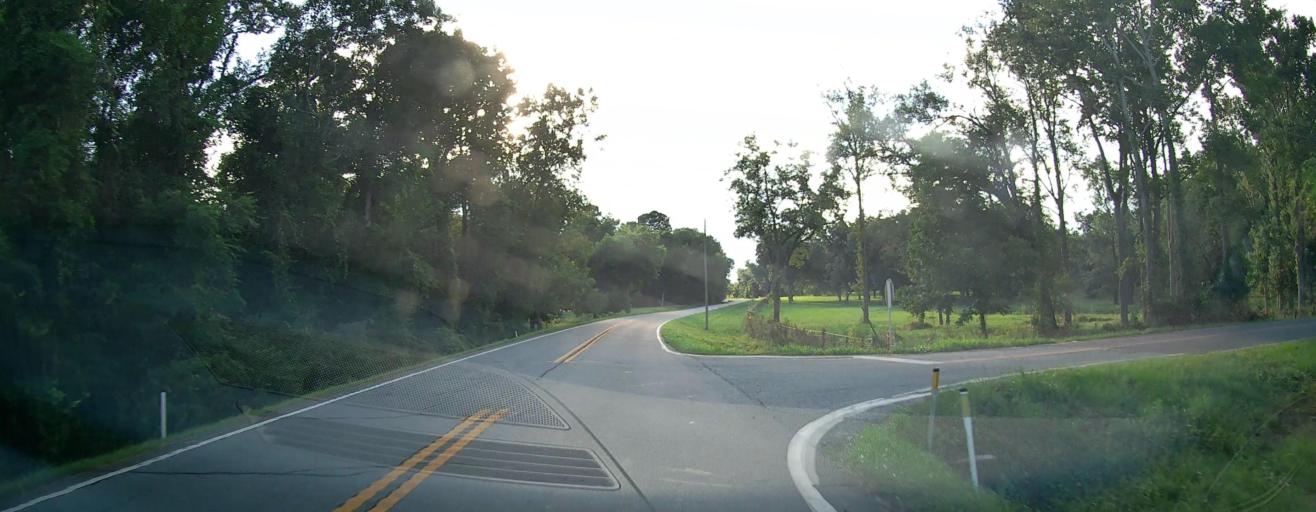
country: US
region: Georgia
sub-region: Pulaski County
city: Hawkinsville
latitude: 32.2679
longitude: -83.5379
